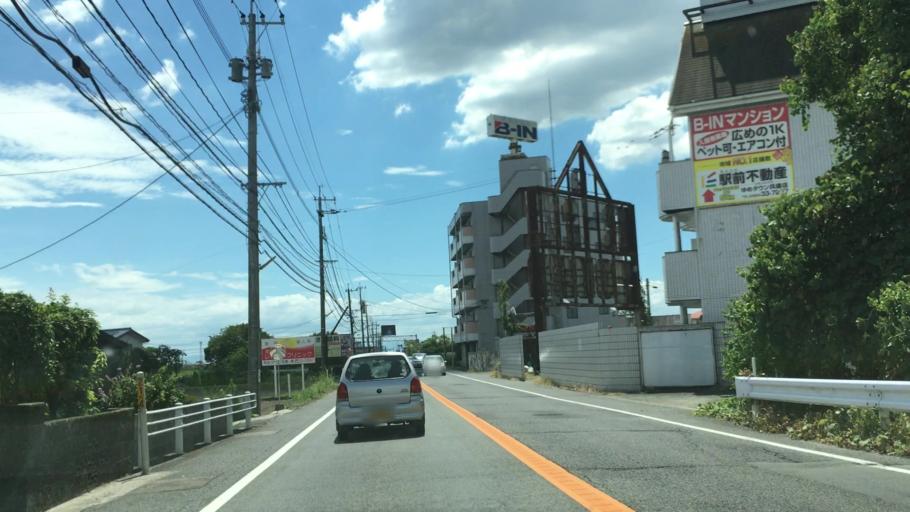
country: JP
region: Saga Prefecture
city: Kanzakimachi-kanzaki
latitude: 33.2907
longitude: 130.3541
